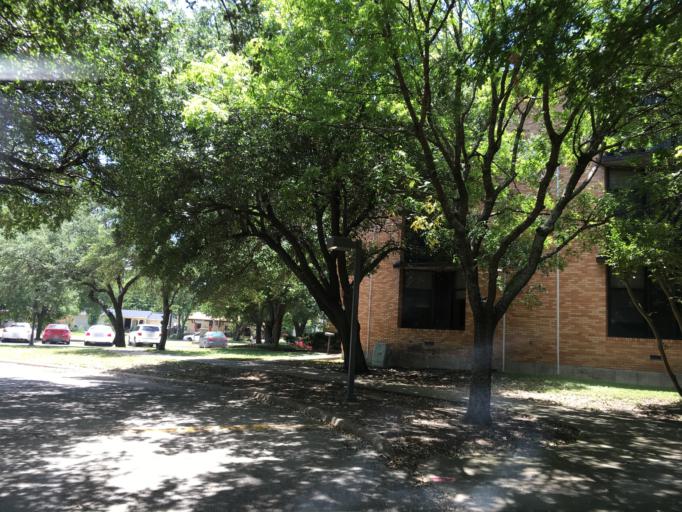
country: US
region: Texas
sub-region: Dallas County
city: Garland
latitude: 32.8440
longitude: -96.6684
